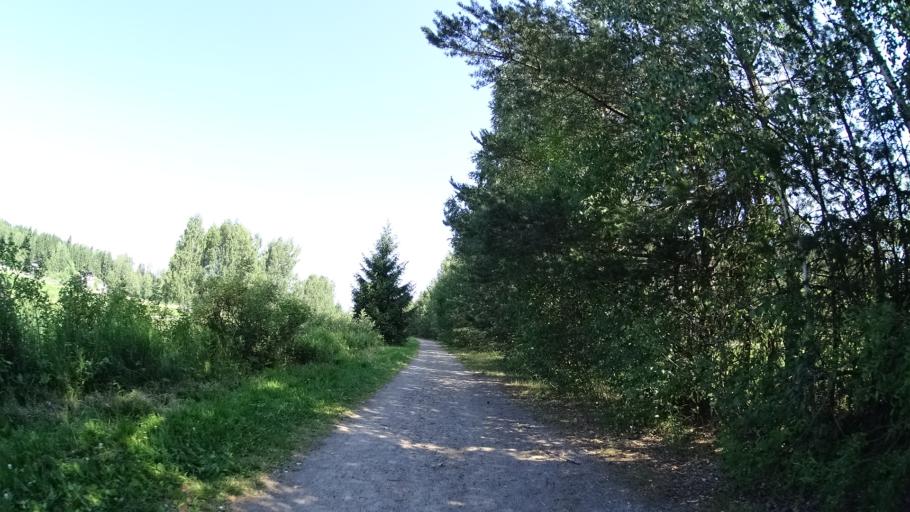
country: FI
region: Uusimaa
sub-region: Helsinki
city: Kerava
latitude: 60.3493
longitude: 25.1264
